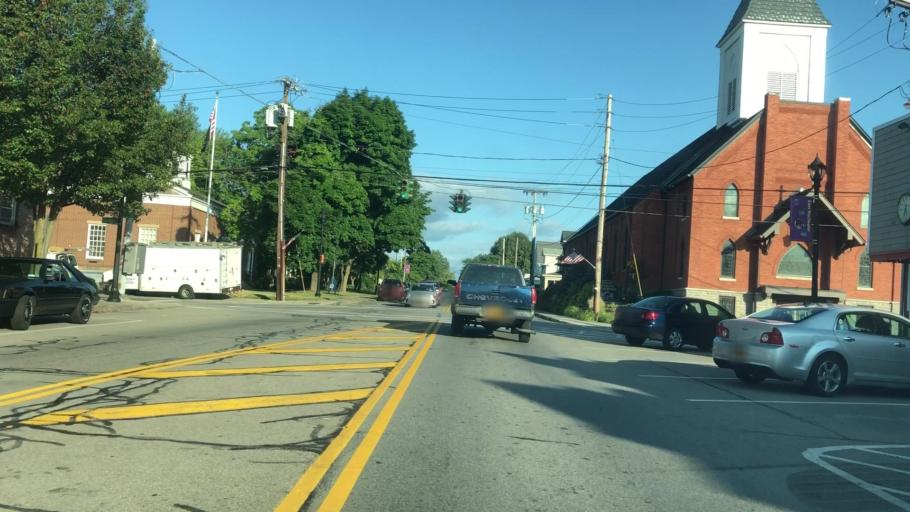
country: US
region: New York
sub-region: Monroe County
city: East Rochester
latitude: 43.1136
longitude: -77.4875
